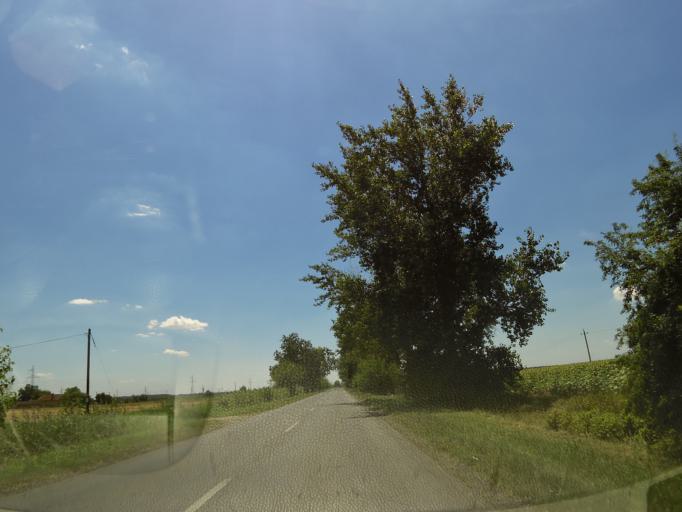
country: HU
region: Csongrad
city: Sandorfalva
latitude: 46.3321
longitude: 20.1337
